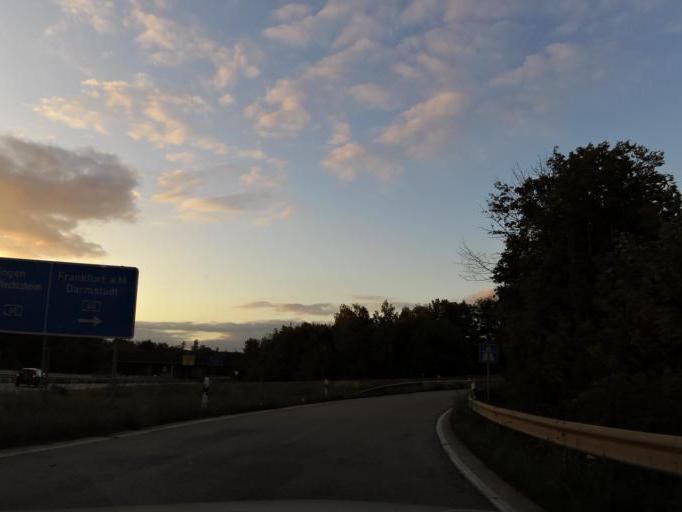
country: DE
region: Hesse
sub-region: Regierungsbezirk Darmstadt
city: Ginsheim-Gustavsburg
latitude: 49.9692
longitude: 8.3134
